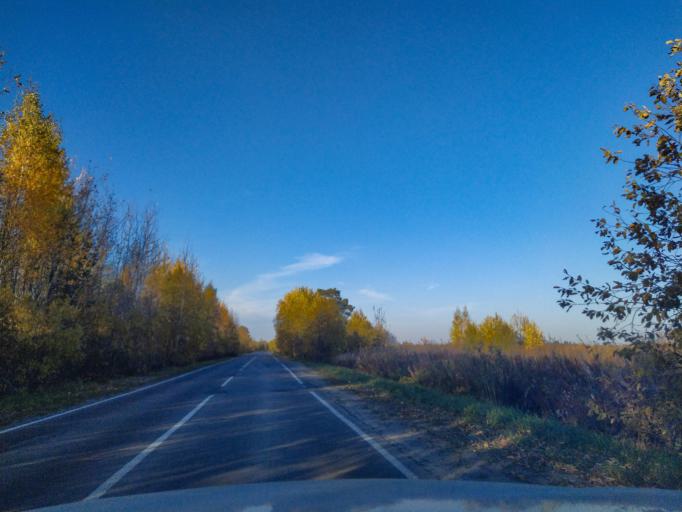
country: RU
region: Leningrad
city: Siverskiy
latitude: 59.3137
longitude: 30.0330
